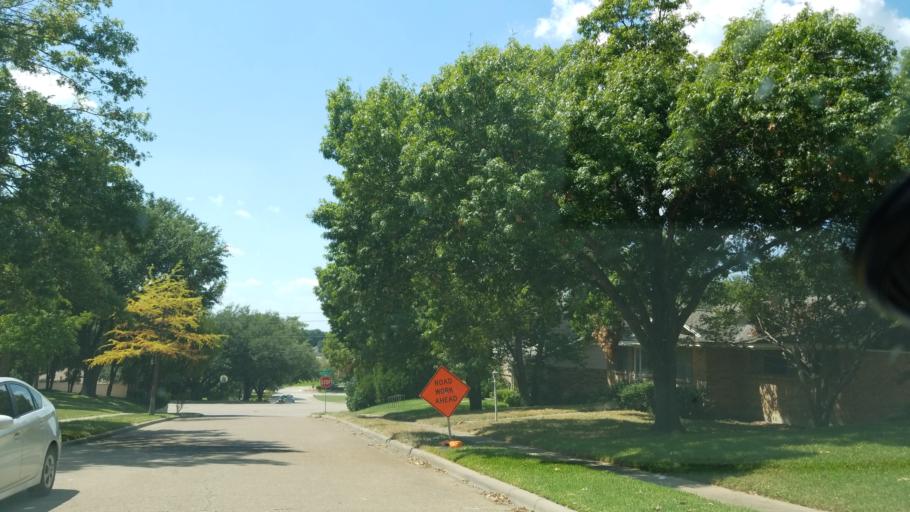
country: US
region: Texas
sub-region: Dallas County
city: Richardson
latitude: 32.8846
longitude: -96.7170
